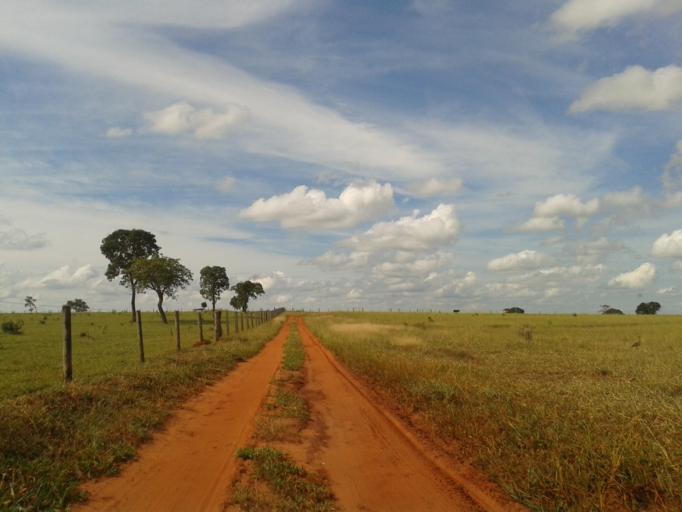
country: BR
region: Minas Gerais
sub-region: Campina Verde
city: Campina Verde
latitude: -19.4527
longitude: -49.6711
